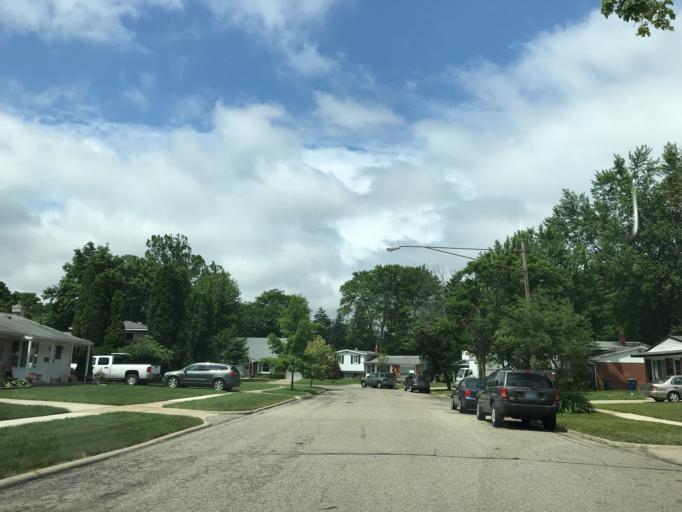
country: US
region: Michigan
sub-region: Washtenaw County
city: Ann Arbor
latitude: 42.2388
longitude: -83.7058
